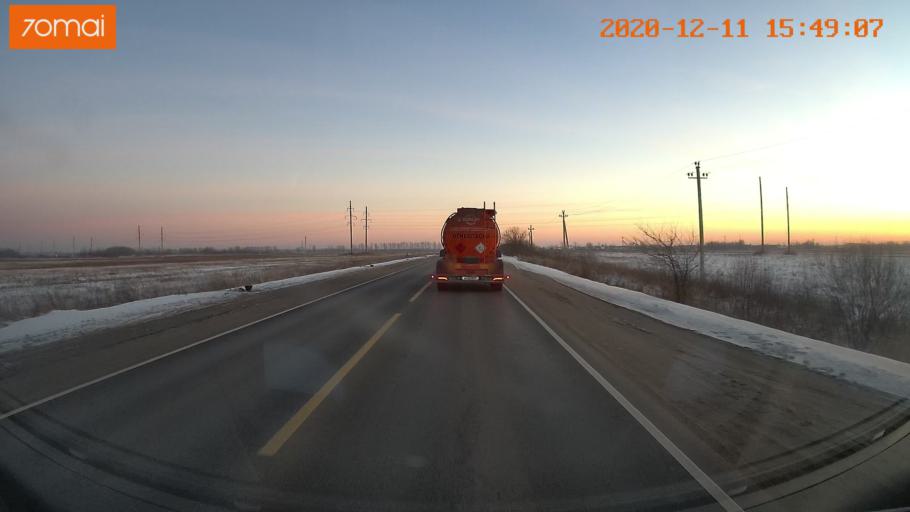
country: RU
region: Ivanovo
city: Novo-Talitsy
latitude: 56.9900
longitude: 40.8721
